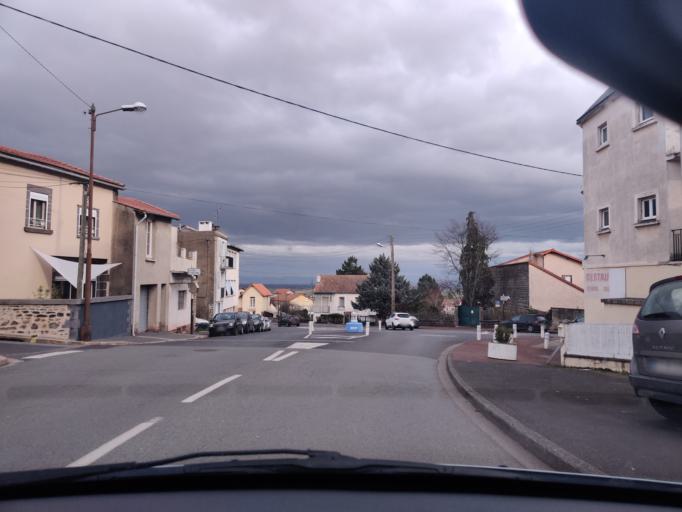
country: FR
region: Auvergne
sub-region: Departement du Puy-de-Dome
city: Chatel-Guyon
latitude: 45.9236
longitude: 3.0692
